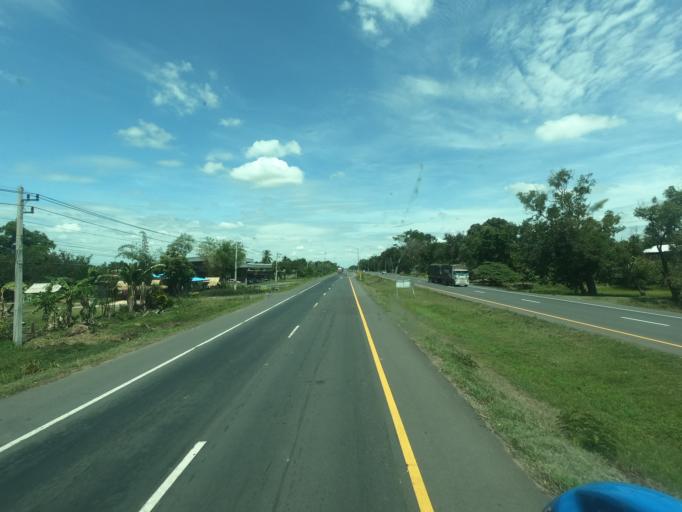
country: TH
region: Surin
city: Prasat
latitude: 14.6097
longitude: 103.3177
